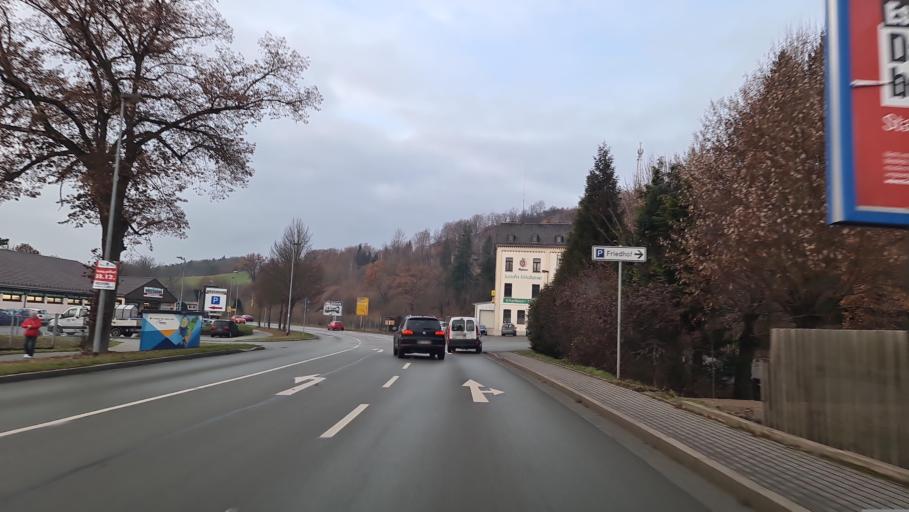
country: DE
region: Saxony
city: Mylau
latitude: 50.6217
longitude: 12.2631
